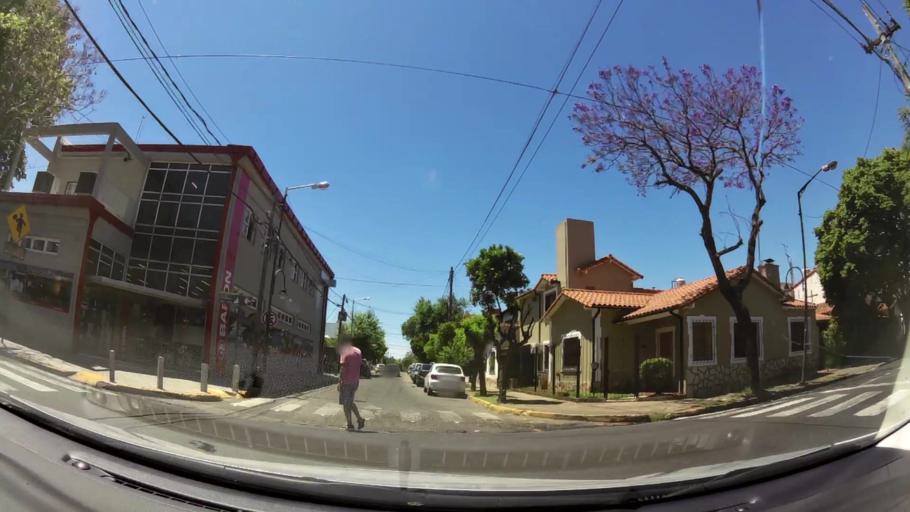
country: AR
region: Buenos Aires
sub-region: Partido de Tigre
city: Tigre
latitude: -34.4447
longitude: -58.5490
